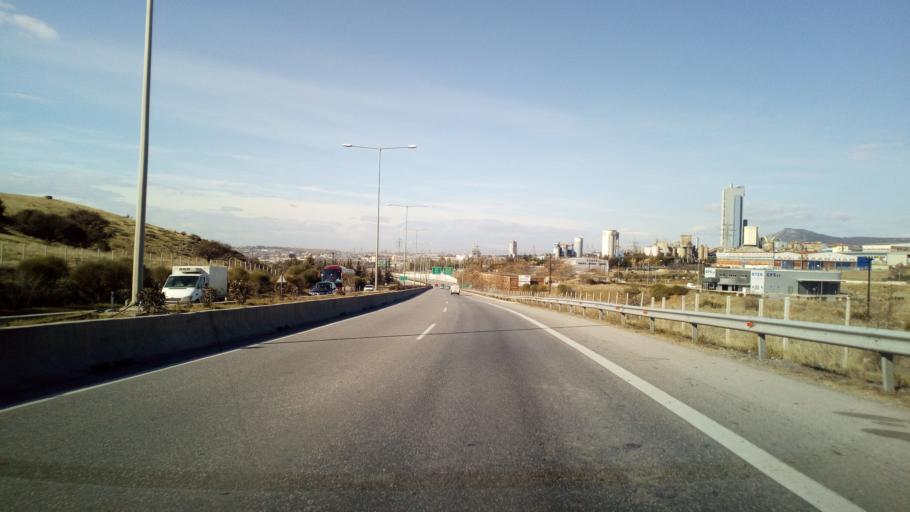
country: GR
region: Central Macedonia
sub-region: Nomos Thessalonikis
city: Efkarpia
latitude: 40.6945
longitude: 22.9625
